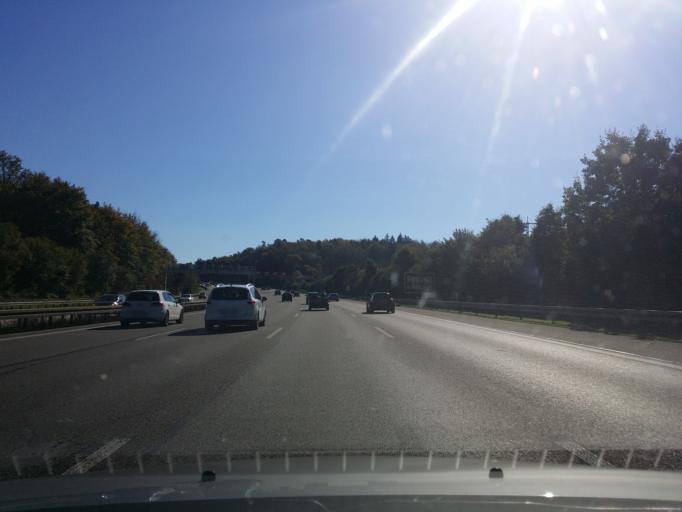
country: DE
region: Baden-Wuerttemberg
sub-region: Regierungsbezirk Stuttgart
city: Sindelfingen
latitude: 48.7430
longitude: 9.0350
